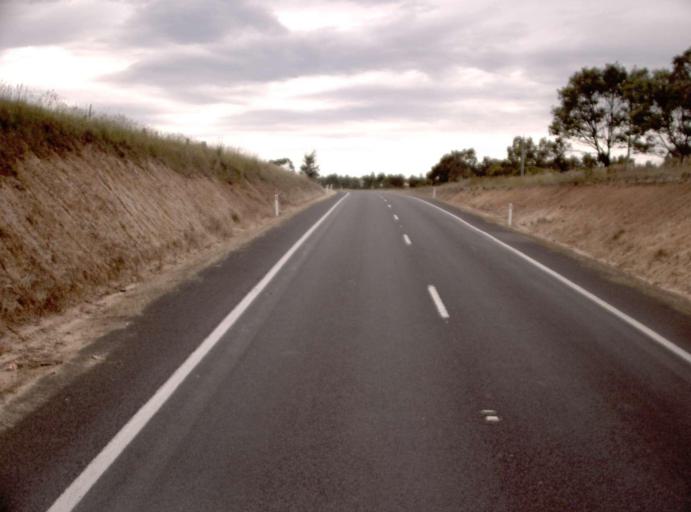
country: AU
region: Victoria
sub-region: Wellington
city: Sale
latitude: -38.2885
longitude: 147.0360
